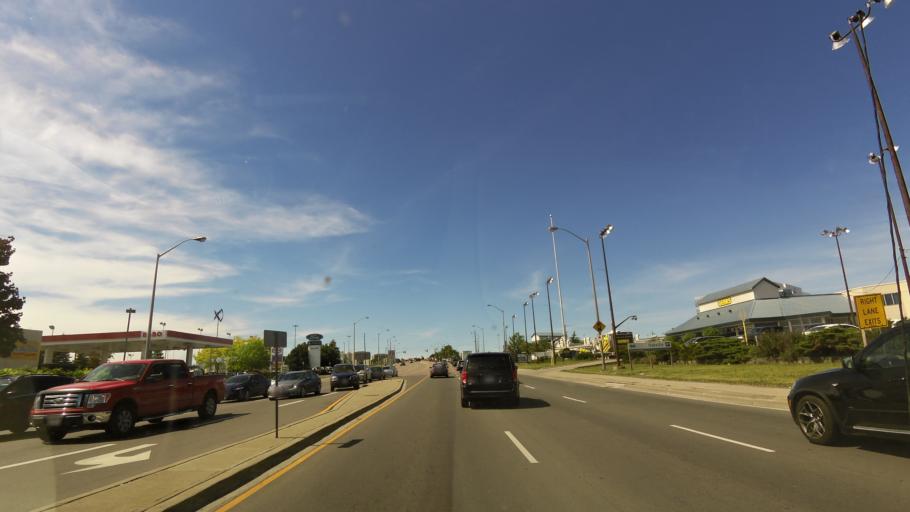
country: CA
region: Ontario
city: Oakville
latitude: 43.4577
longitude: -79.6815
